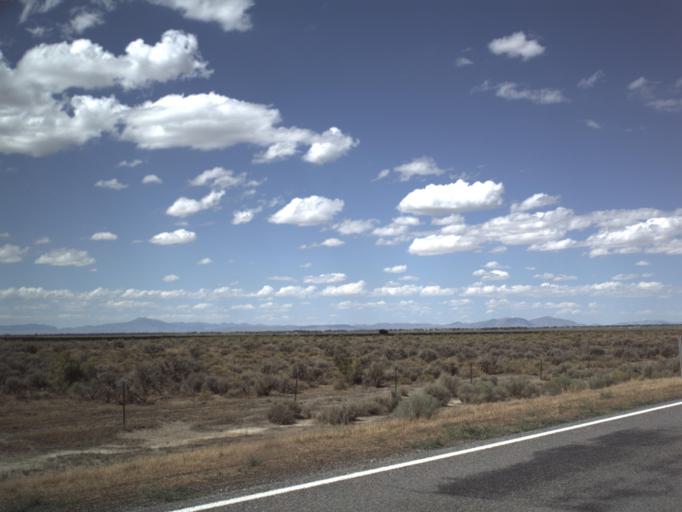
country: US
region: Utah
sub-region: Millard County
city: Delta
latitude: 39.2653
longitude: -112.4506
